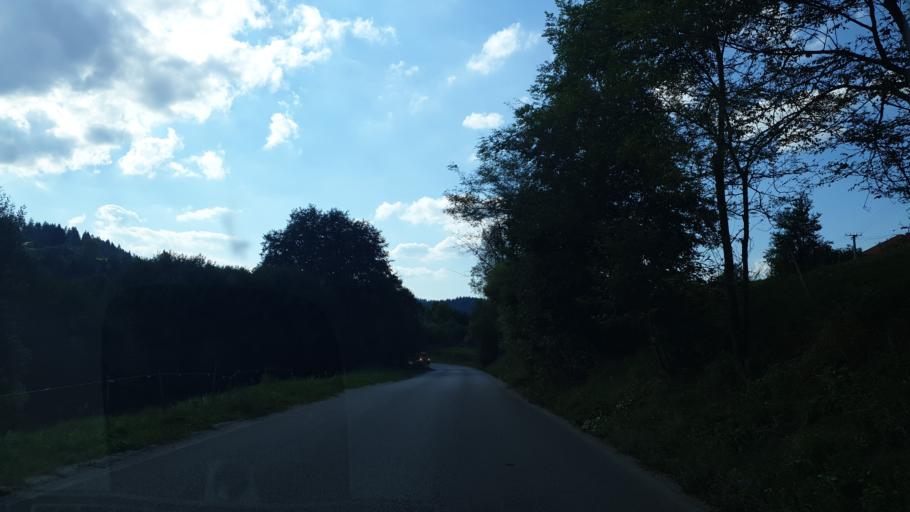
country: RS
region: Central Serbia
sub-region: Zlatiborski Okrug
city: Nova Varos
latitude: 43.4376
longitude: 19.8672
